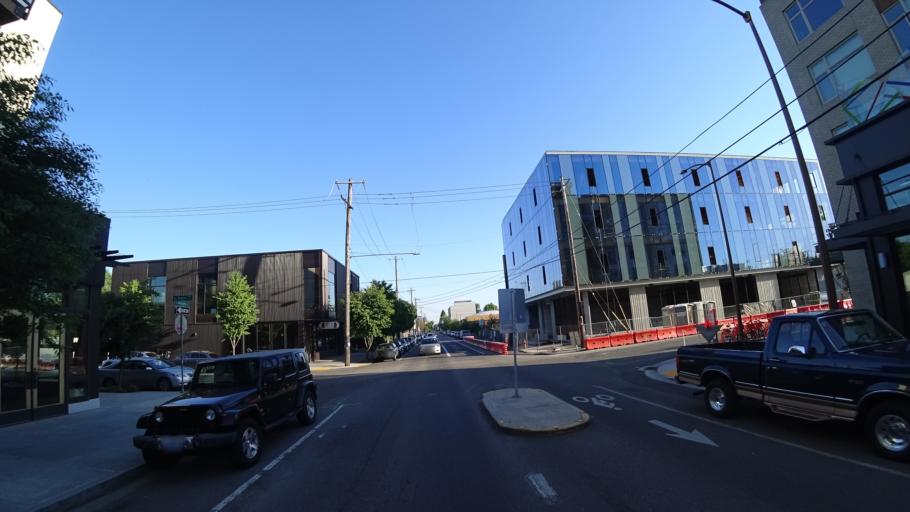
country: US
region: Oregon
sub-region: Multnomah County
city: Portland
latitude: 45.5535
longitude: -122.6667
